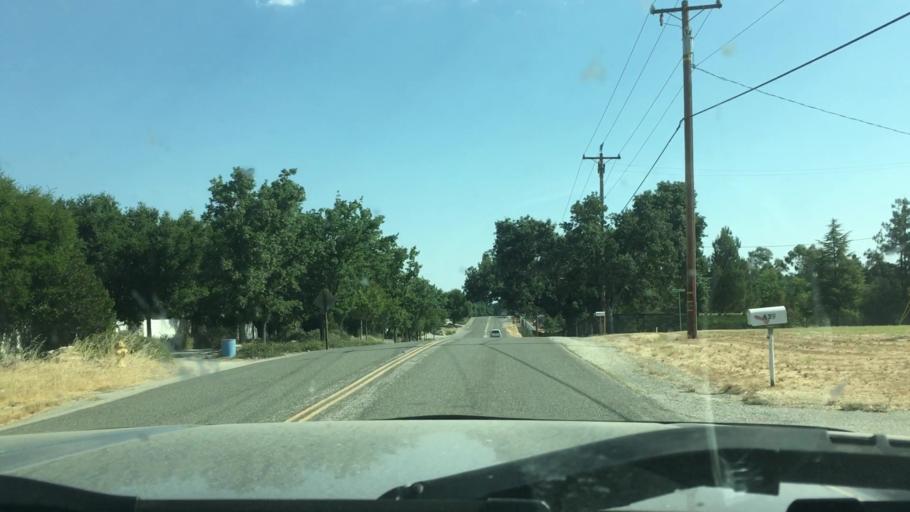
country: US
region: California
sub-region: San Luis Obispo County
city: Templeton
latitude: 35.5484
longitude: -120.7291
